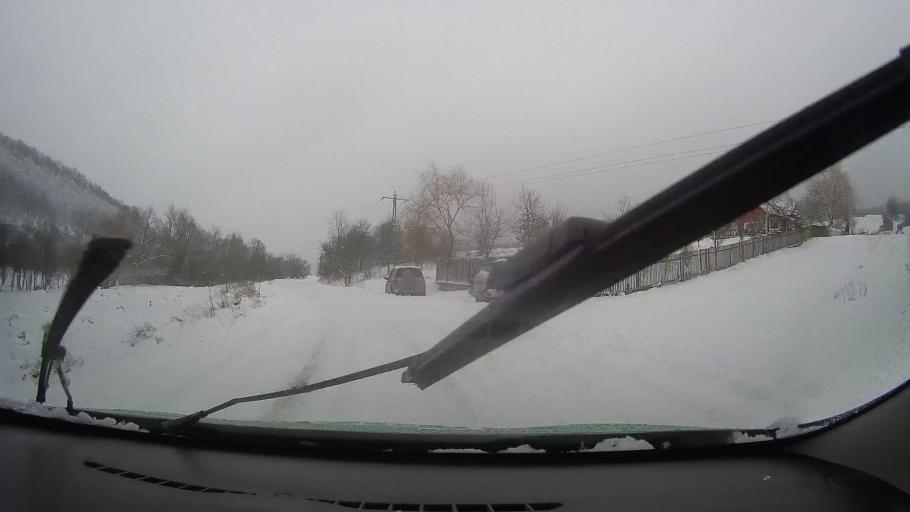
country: RO
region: Hunedoara
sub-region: Comuna Carjiti
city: Carjiti
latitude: 45.8422
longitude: 22.8335
